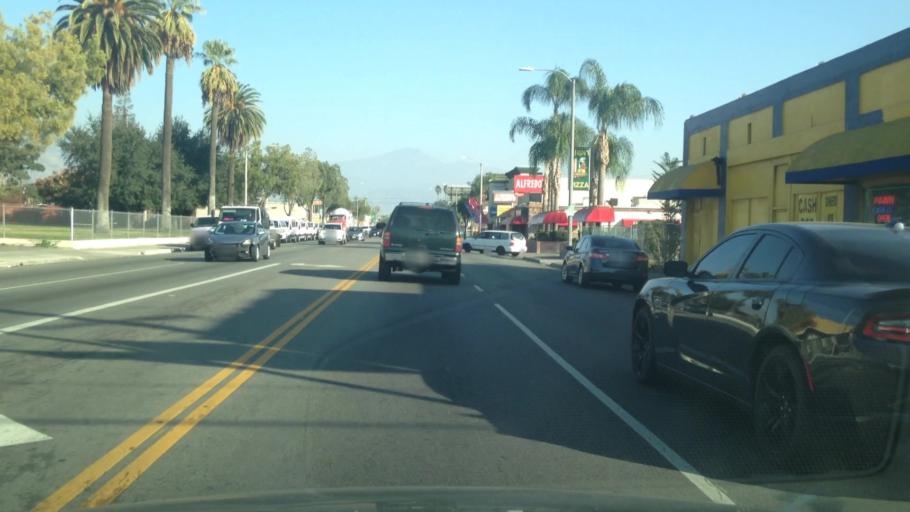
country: US
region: California
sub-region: San Bernardino County
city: San Bernardino
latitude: 34.1213
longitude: -117.2895
